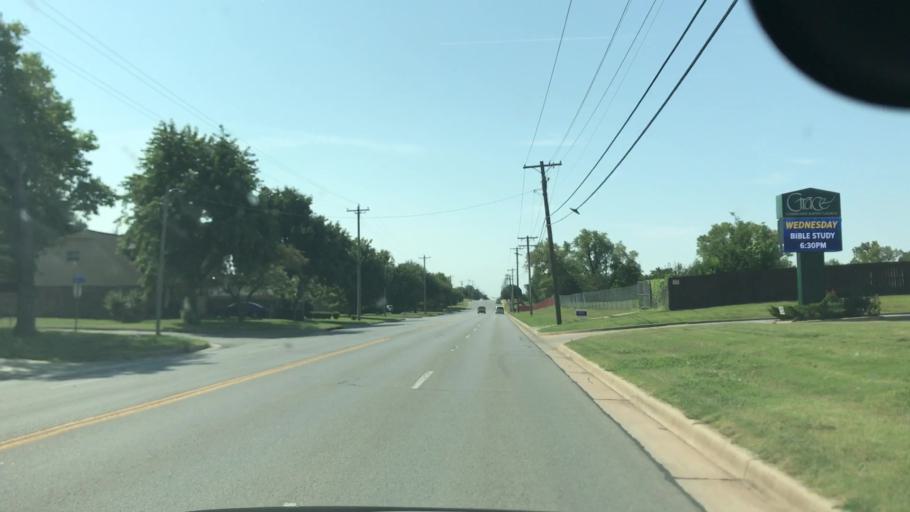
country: US
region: Oklahoma
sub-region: Cleveland County
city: Moore
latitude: 35.3593
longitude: -97.5122
